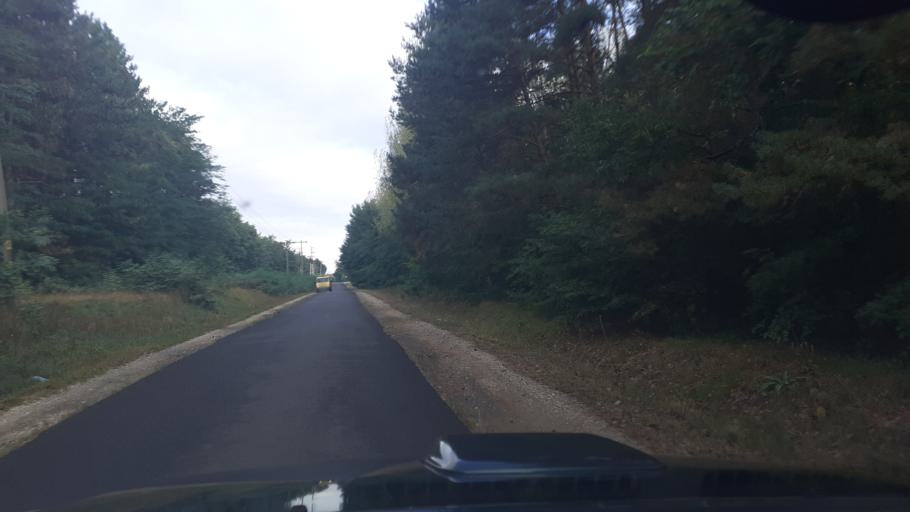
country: HU
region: Fejer
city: dunaujvaros
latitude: 46.9437
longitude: 18.8632
